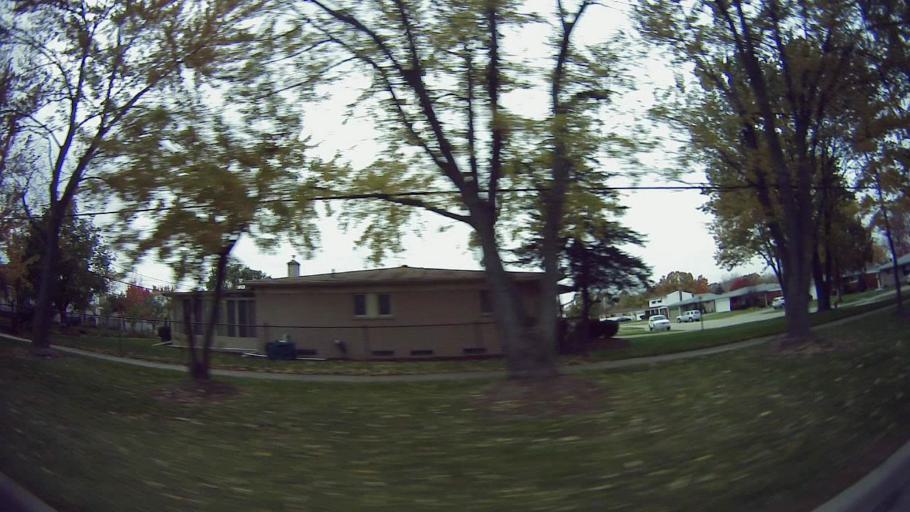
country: US
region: Michigan
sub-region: Macomb County
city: Sterling Heights
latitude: 42.5459
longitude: -83.0691
